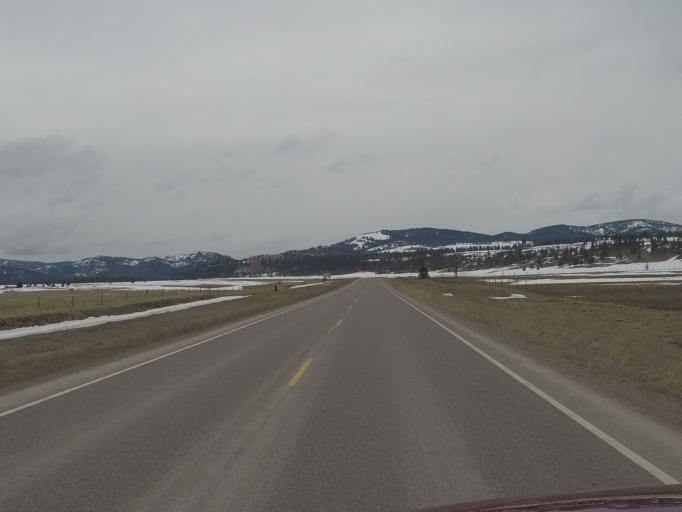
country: US
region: Montana
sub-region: Missoula County
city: Seeley Lake
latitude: 47.0151
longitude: -113.3719
